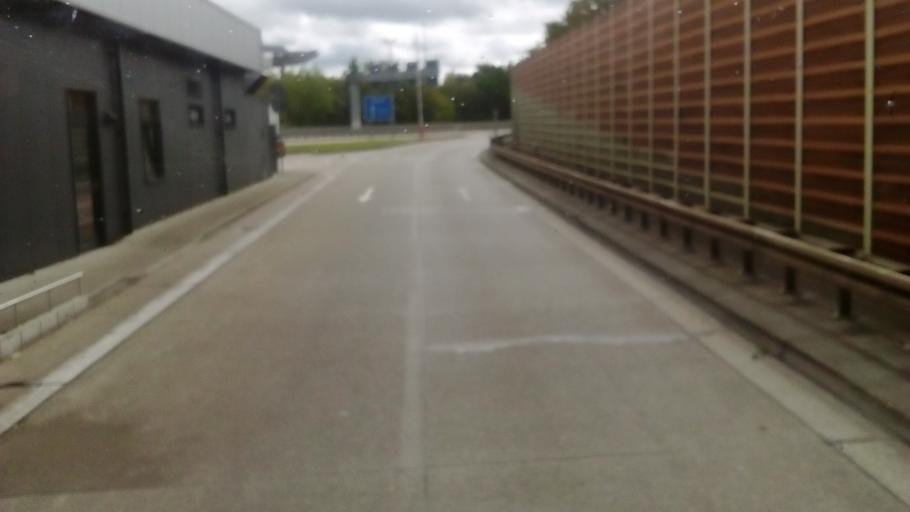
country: DE
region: Baden-Wuerttemberg
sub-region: Freiburg Region
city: Weil am Rhein
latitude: 47.5937
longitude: 7.6032
